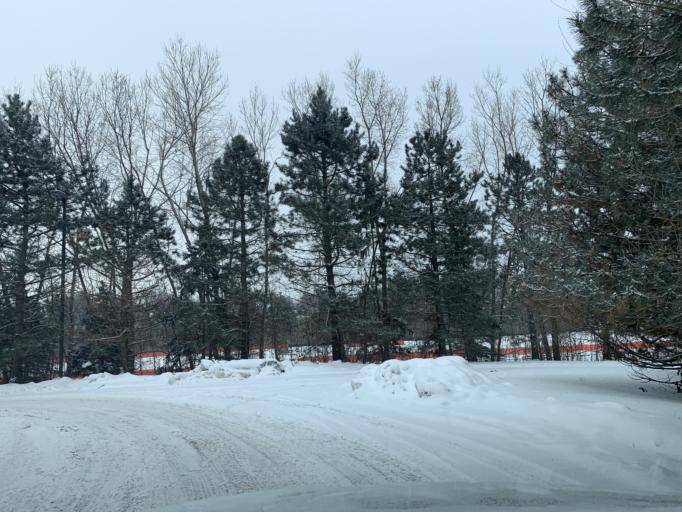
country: US
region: Minnesota
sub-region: Hennepin County
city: Saint Louis Park
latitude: 44.9460
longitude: -93.3327
